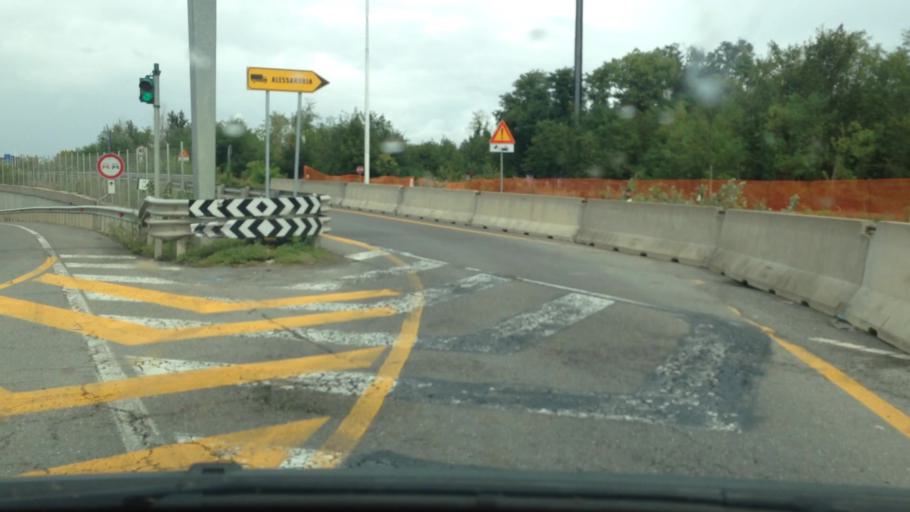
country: IT
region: Piedmont
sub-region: Provincia di Alessandria
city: Tortona
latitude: 44.9055
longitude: 8.8375
